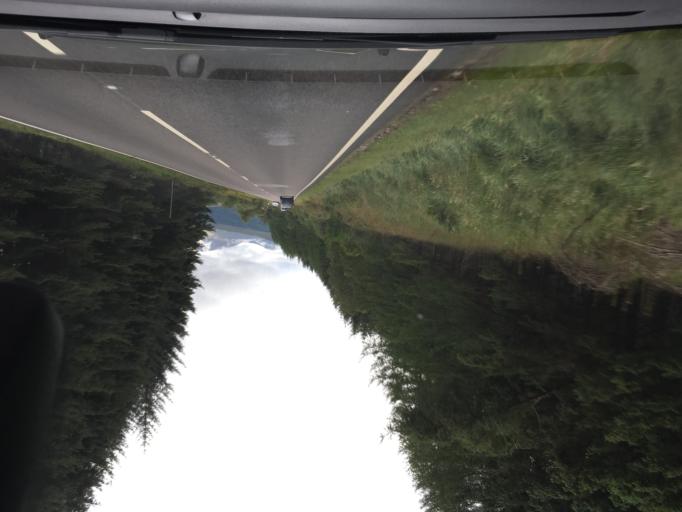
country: GB
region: Scotland
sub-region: Argyll and Bute
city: Garelochhead
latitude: 56.4822
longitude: -4.7366
